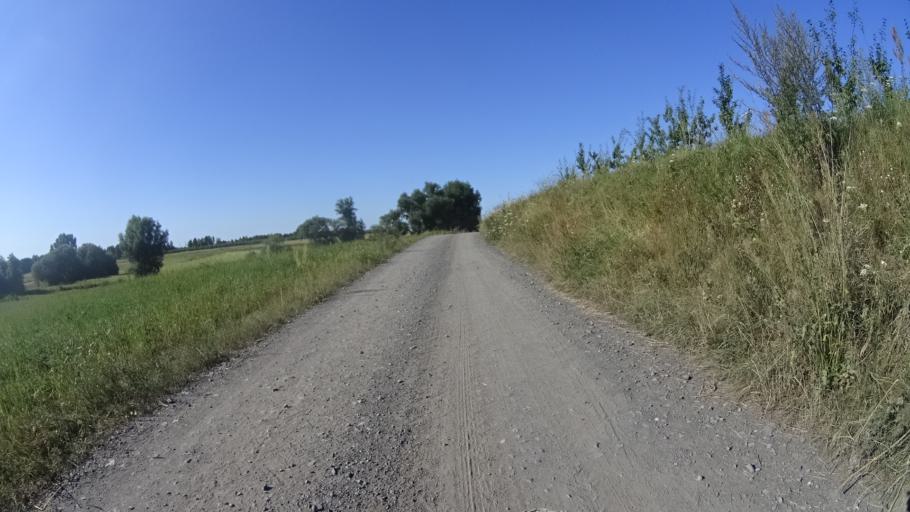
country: PL
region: Masovian Voivodeship
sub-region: Powiat bialobrzeski
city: Wysmierzyce
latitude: 51.6700
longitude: 20.8489
